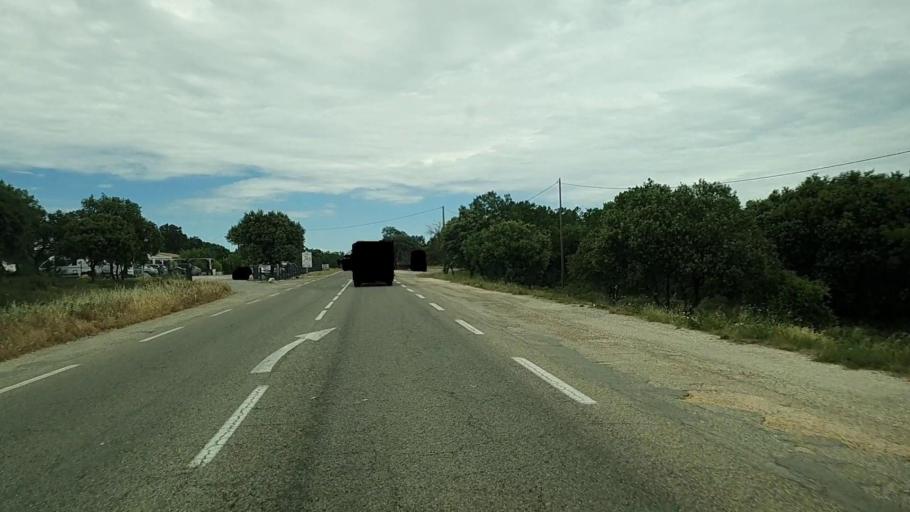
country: FR
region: Languedoc-Roussillon
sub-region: Departement du Gard
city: Connaux
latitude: 44.0524
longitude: 4.5722
